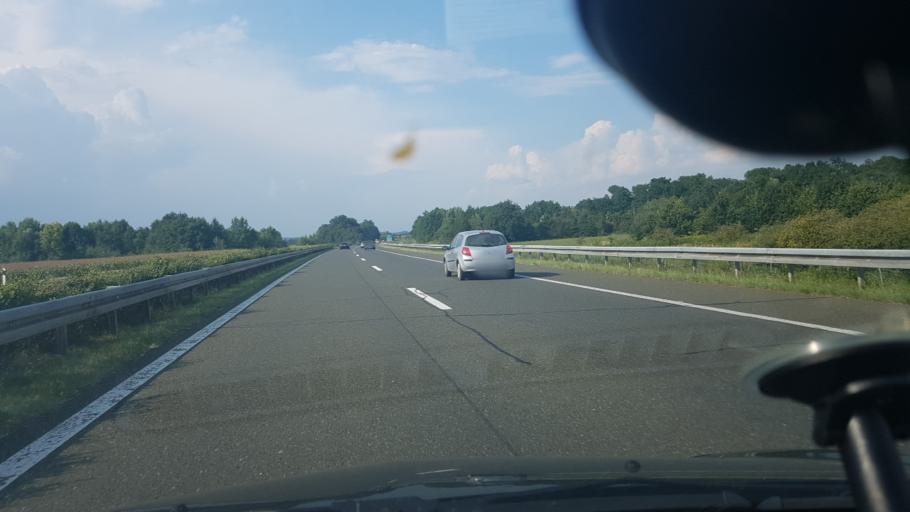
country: HR
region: Zagrebacka
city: Pojatno
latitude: 45.9039
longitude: 15.8205
